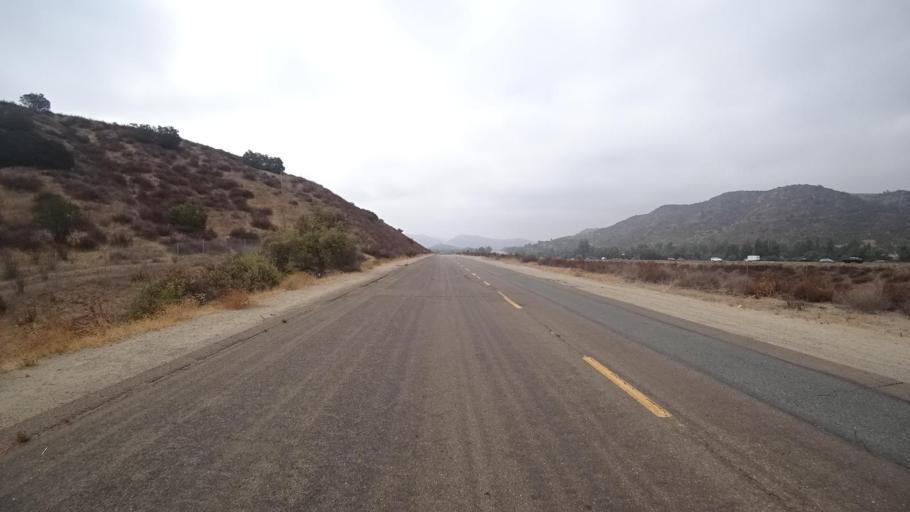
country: US
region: California
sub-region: San Diego County
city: Rainbow
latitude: 33.3626
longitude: -117.1584
